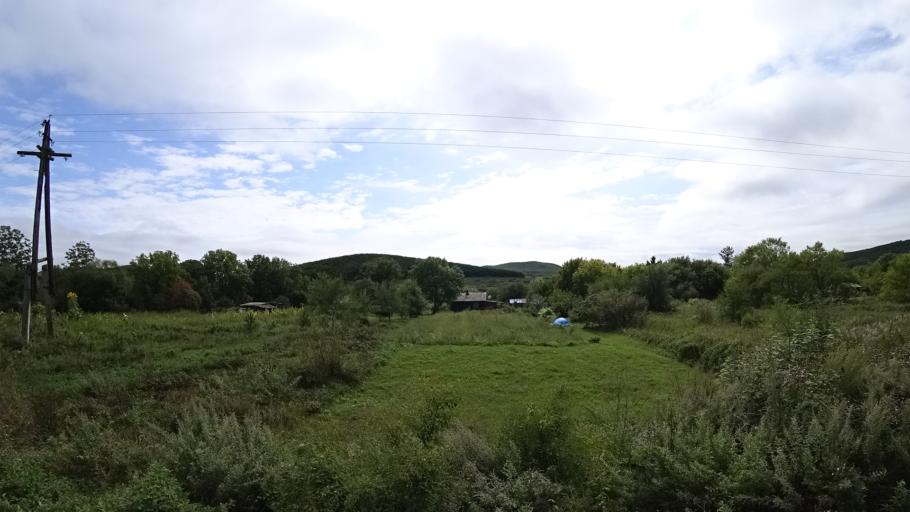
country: RU
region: Primorskiy
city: Lyalichi
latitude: 44.1400
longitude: 132.3821
